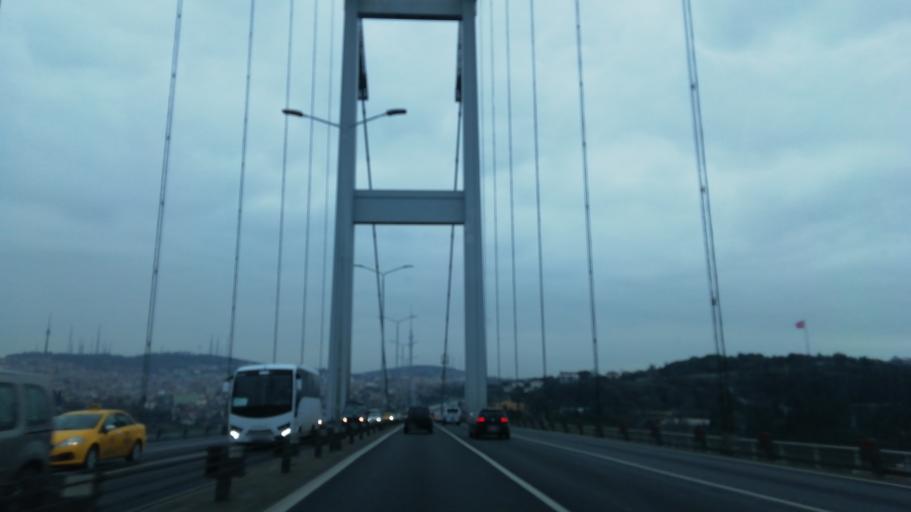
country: TR
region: Istanbul
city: UEskuedar
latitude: 41.0429
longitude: 29.0370
